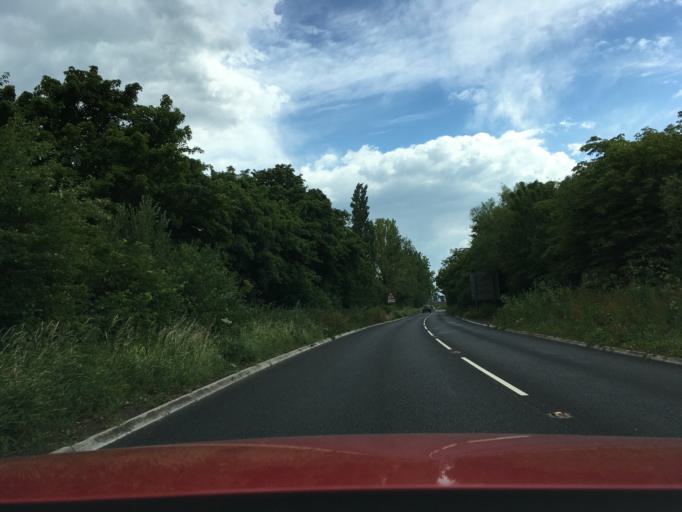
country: GB
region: England
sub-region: Gloucestershire
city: Stonehouse
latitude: 51.7916
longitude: -2.2881
